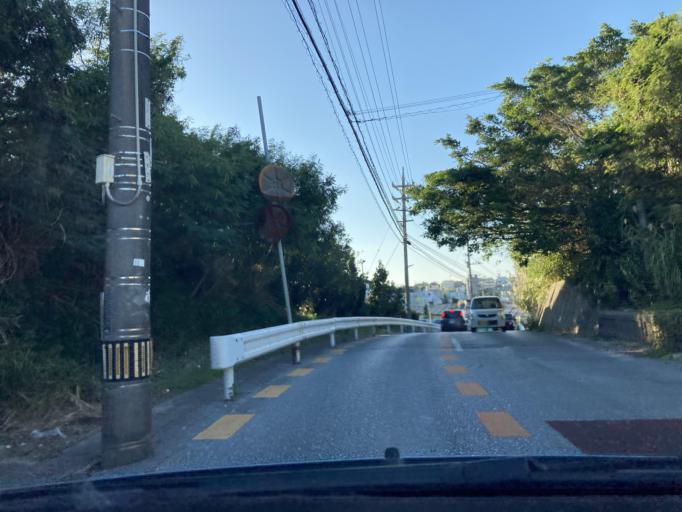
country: JP
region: Okinawa
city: Naha-shi
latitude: 26.2107
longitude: 127.7308
